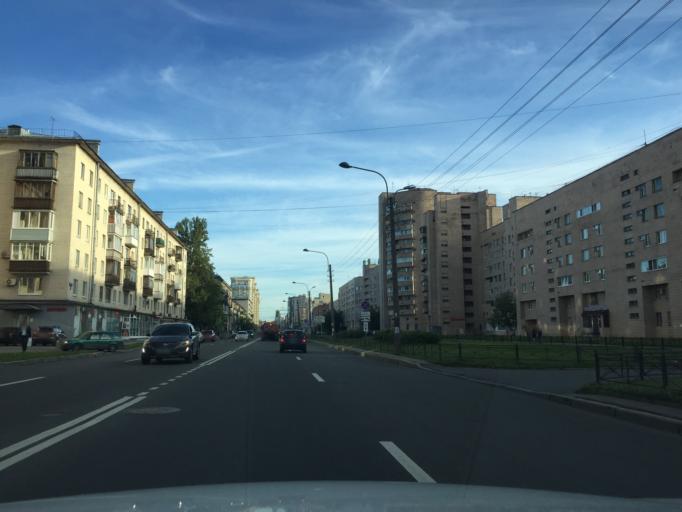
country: RU
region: St.-Petersburg
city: Kupchino
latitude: 59.8632
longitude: 30.3141
